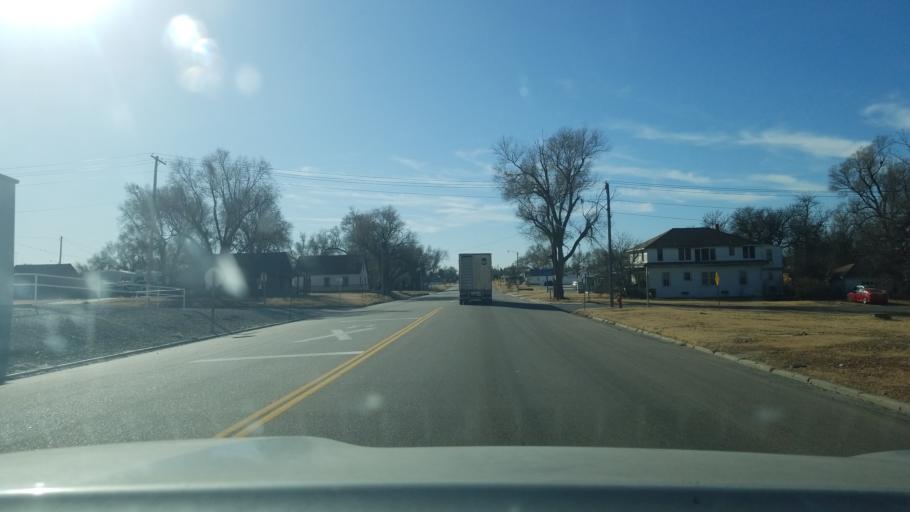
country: US
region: Kansas
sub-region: Ness County
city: Ness City
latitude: 38.4512
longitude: -99.9051
